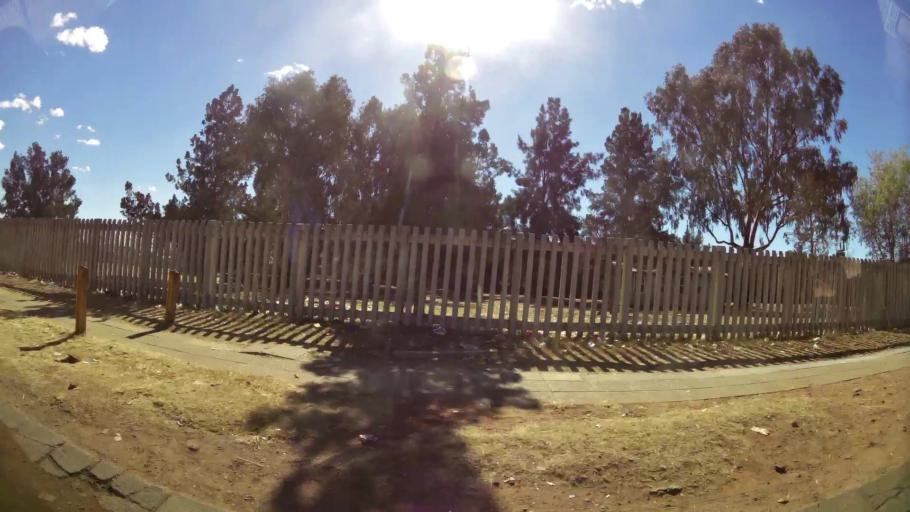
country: ZA
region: North-West
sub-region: Dr Kenneth Kaunda District Municipality
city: Klerksdorp
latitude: -26.8726
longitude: 26.5875
